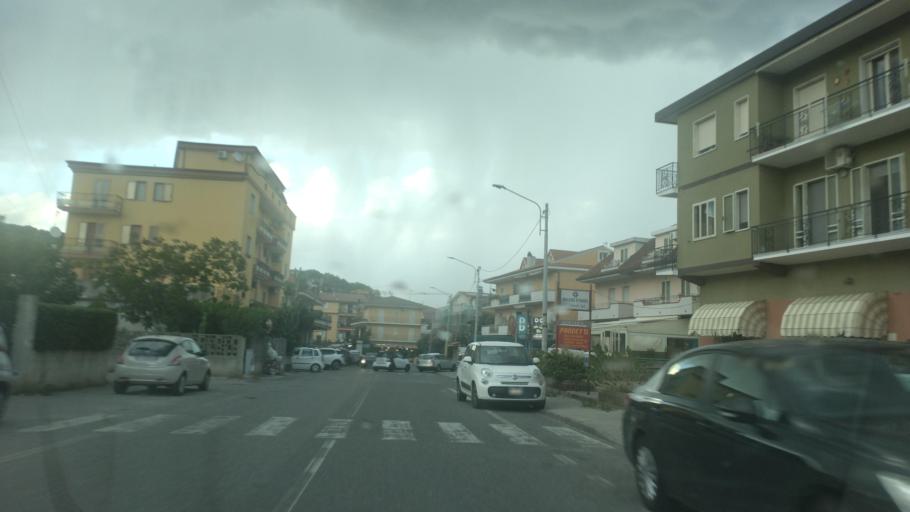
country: IT
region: Calabria
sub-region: Provincia di Catanzaro
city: Montepaone Lido
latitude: 38.7302
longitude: 16.5359
